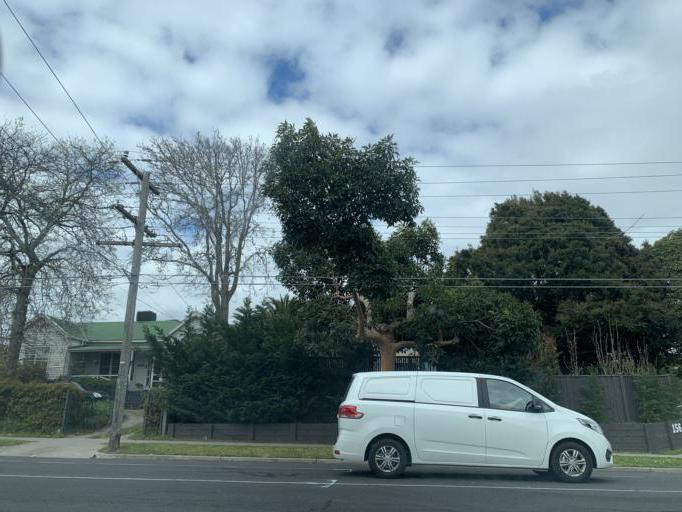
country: AU
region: Victoria
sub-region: Bayside
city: Cheltenham
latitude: -37.9753
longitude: 145.0538
